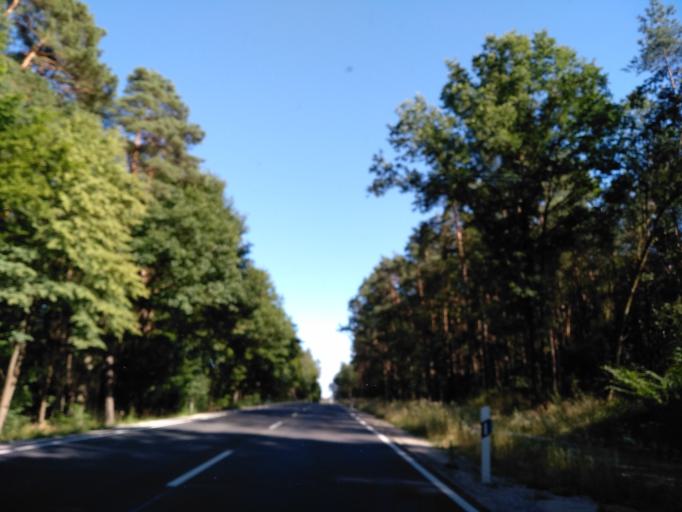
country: DE
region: Bavaria
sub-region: Regierungsbezirk Mittelfranken
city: Hessdorf
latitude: 49.6414
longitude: 10.9257
